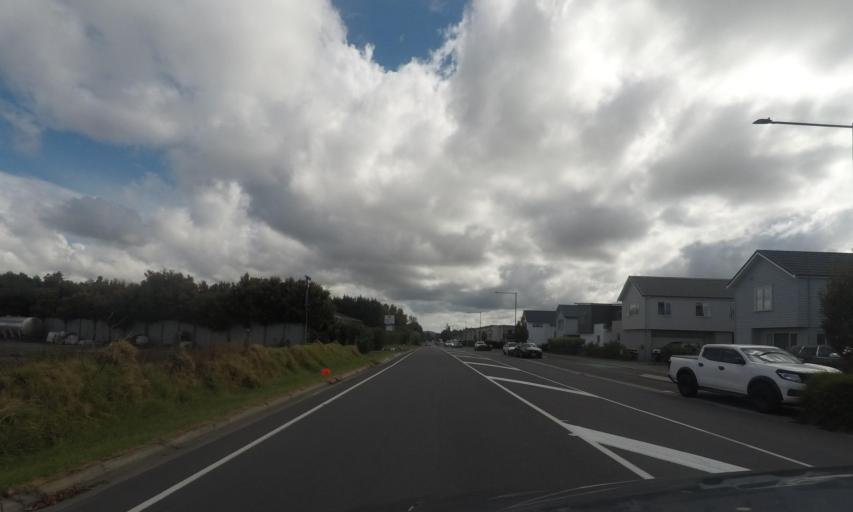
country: NZ
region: Auckland
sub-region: Auckland
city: Rosebank
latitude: -36.7930
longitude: 174.6114
